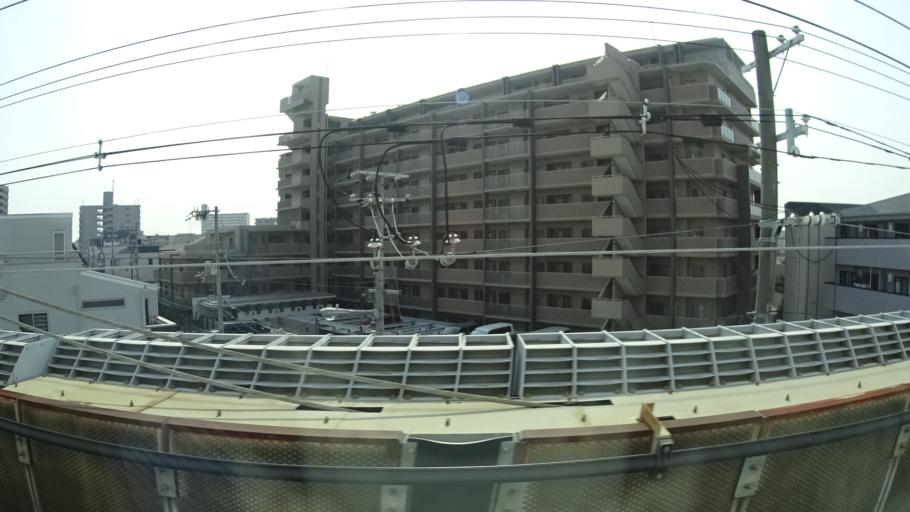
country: JP
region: Osaka
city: Suita
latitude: 34.7397
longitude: 135.5110
